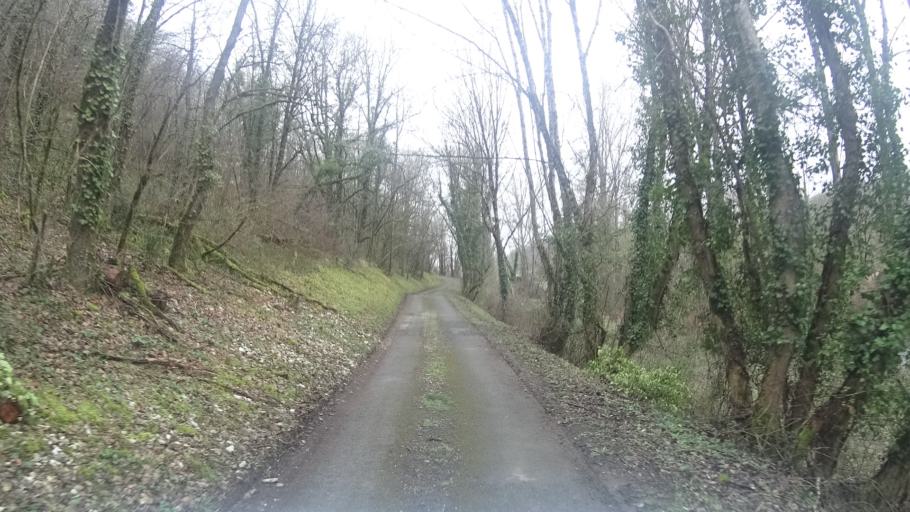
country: FR
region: Aquitaine
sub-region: Departement de la Dordogne
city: Terrasson-Lavilledieu
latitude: 45.1094
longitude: 1.2390
